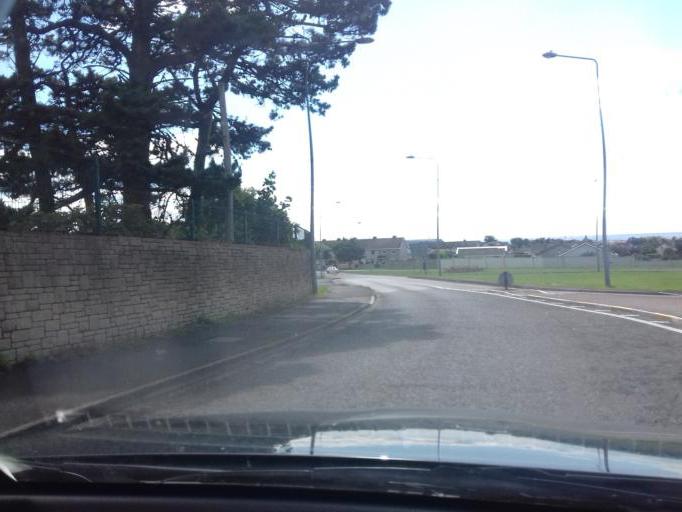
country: IE
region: Munster
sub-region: Waterford
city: Tra Mhor
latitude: 52.1687
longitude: -7.1434
